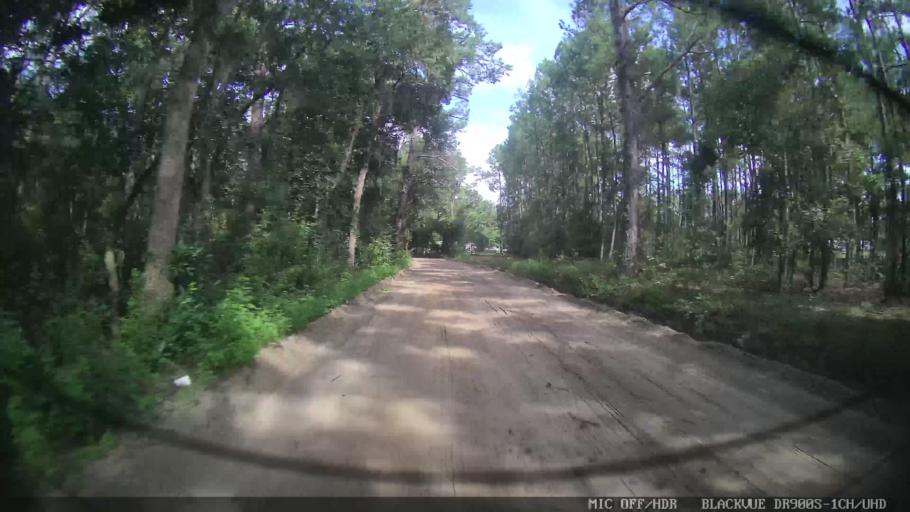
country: US
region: Georgia
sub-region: Echols County
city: Statenville
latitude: 30.6216
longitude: -83.2091
